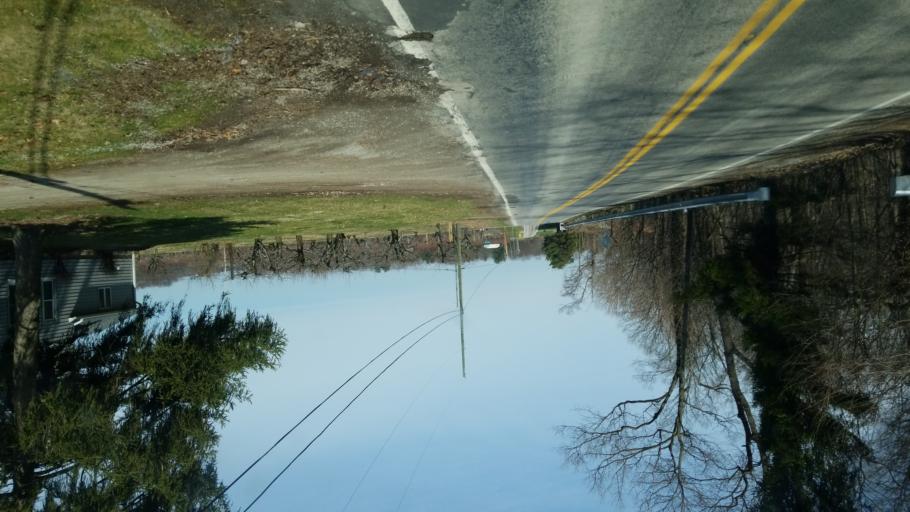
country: US
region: Ohio
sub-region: Lorain County
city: South Amherst
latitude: 41.3658
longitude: -82.3034
